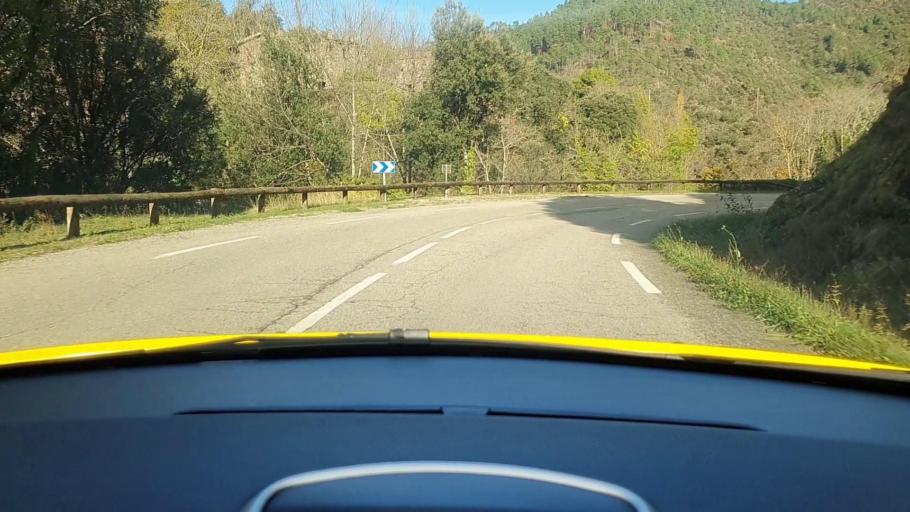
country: FR
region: Languedoc-Roussillon
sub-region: Departement du Gard
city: Valleraugue
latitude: 44.1435
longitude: 3.6986
